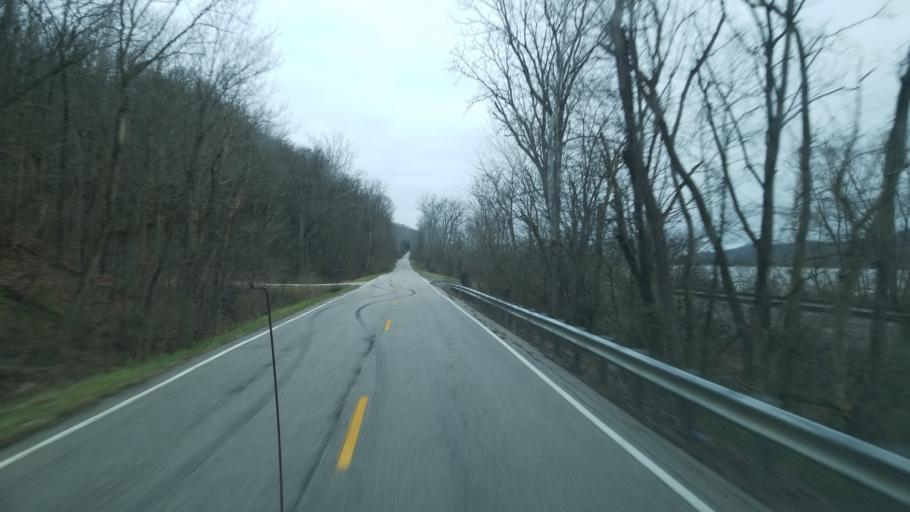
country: US
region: Kentucky
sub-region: Bracken County
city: Augusta
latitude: 38.7666
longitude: -84.0395
